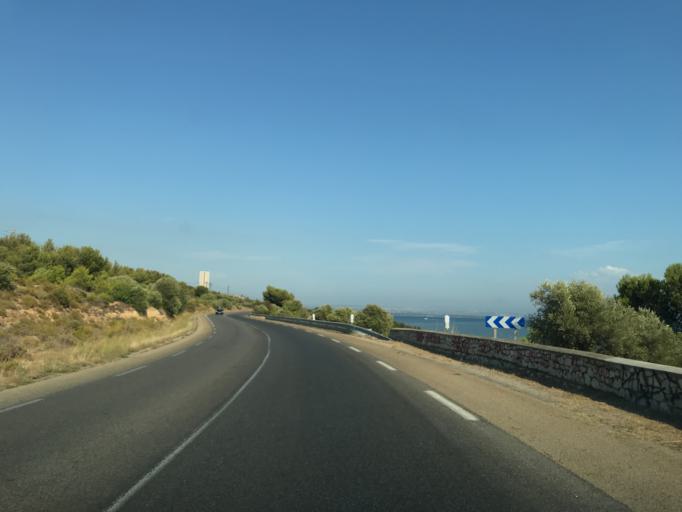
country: FR
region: Provence-Alpes-Cote d'Azur
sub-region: Departement des Bouches-du-Rhone
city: Saint-Chamas
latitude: 43.5283
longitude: 5.0592
